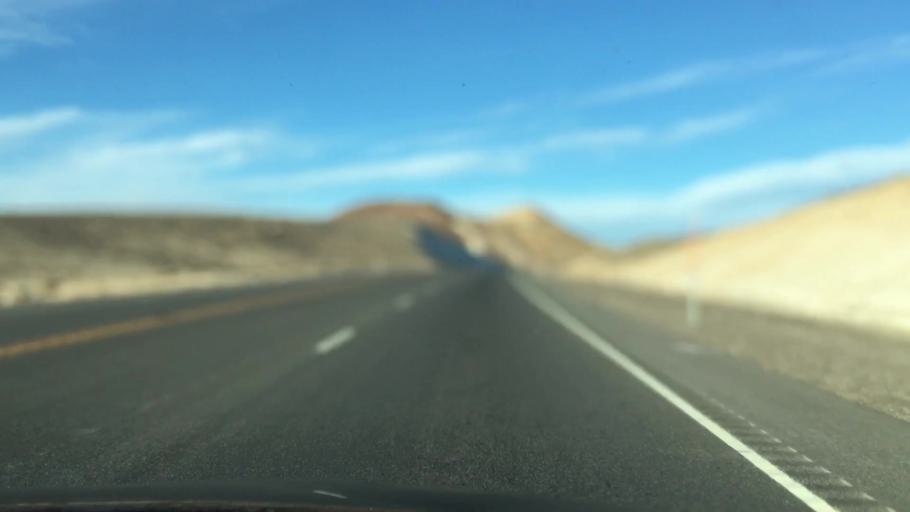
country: US
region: Nevada
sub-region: Nye County
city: Tonopah
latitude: 37.9920
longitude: -117.2727
